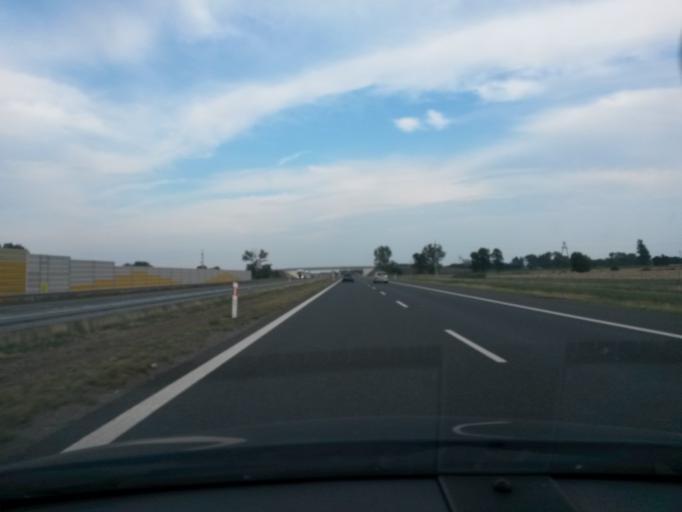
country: PL
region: Lodz Voivodeship
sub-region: Powiat poddebicki
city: Wartkowice
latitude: 52.0067
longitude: 18.9808
